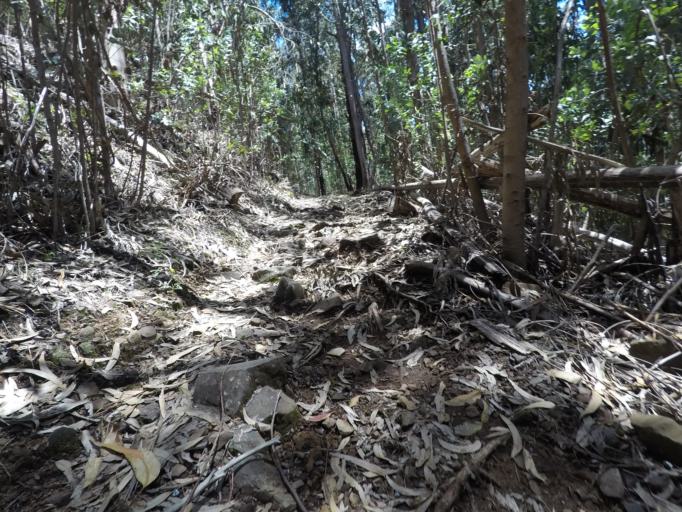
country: PT
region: Madeira
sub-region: Camara de Lobos
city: Curral das Freiras
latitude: 32.7499
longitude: -16.9707
